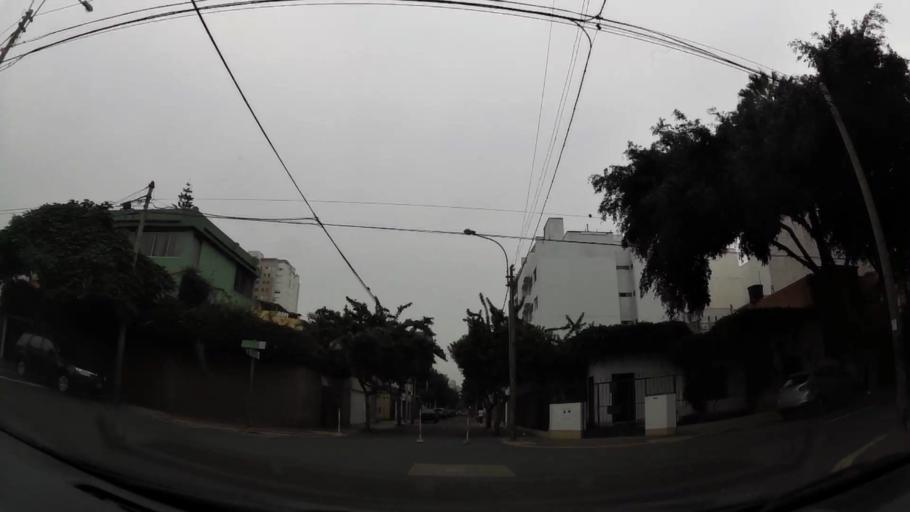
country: PE
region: Lima
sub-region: Lima
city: San Isidro
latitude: -12.1281
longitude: -77.0314
